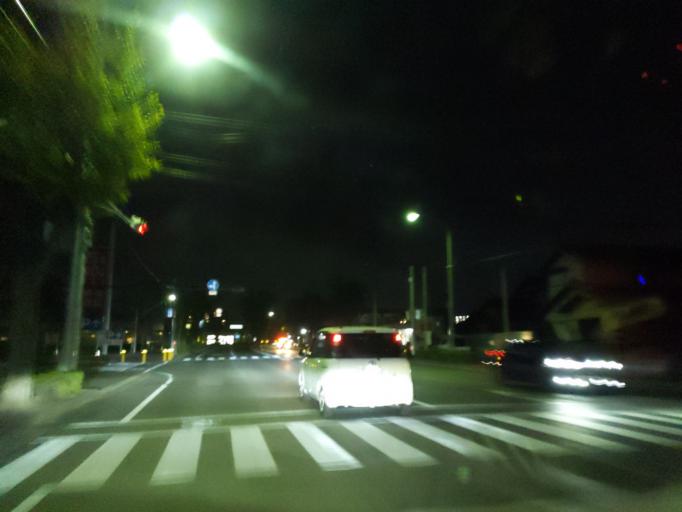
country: JP
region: Okayama
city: Okayama-shi
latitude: 34.6765
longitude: 133.9443
